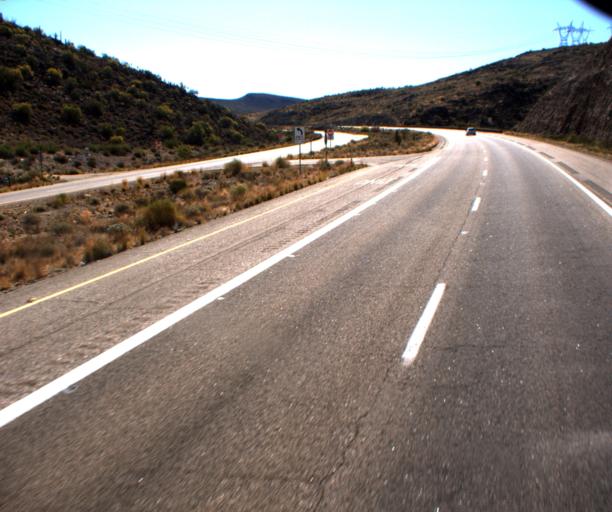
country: US
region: Arizona
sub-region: Yavapai County
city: Bagdad
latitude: 34.5718
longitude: -113.4861
